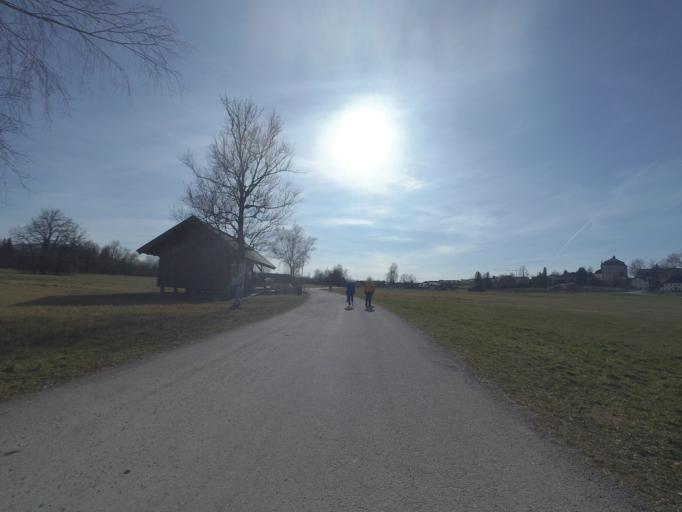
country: AT
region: Salzburg
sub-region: Politischer Bezirk Salzburg-Umgebung
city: Seekirchen am Wallersee
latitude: 47.9024
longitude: 13.1410
